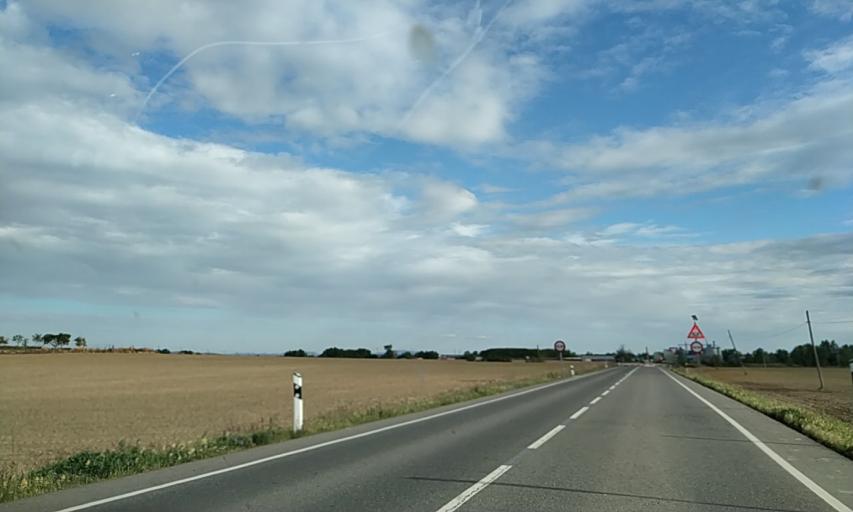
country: ES
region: Extremadura
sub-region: Provincia de Caceres
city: Moraleja
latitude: 40.0864
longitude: -6.6718
